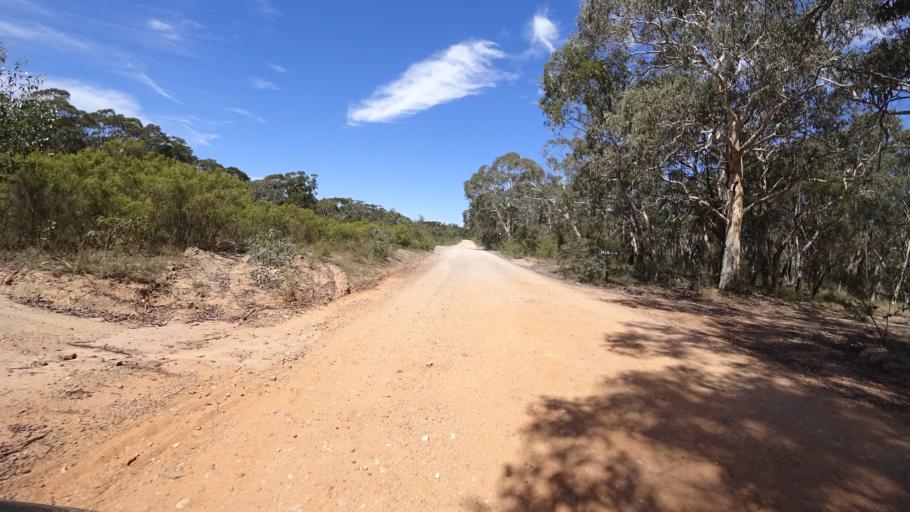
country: AU
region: New South Wales
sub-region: Lithgow
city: Lithgow
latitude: -33.3422
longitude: 150.2532
